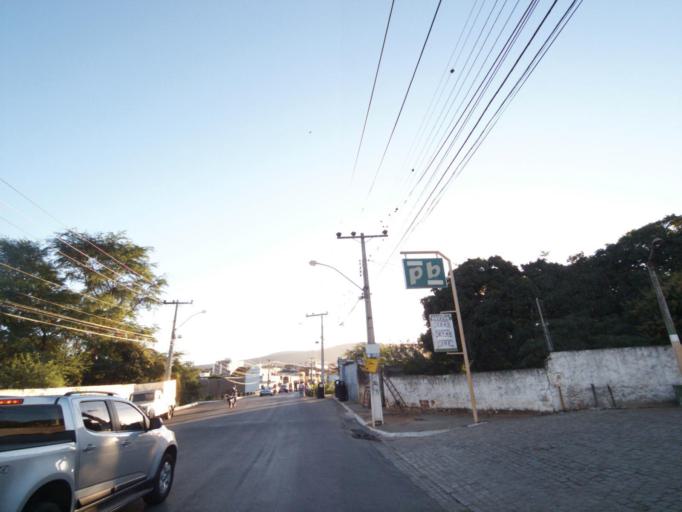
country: BR
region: Bahia
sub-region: Brumado
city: Brumado
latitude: -14.2033
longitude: -41.6609
